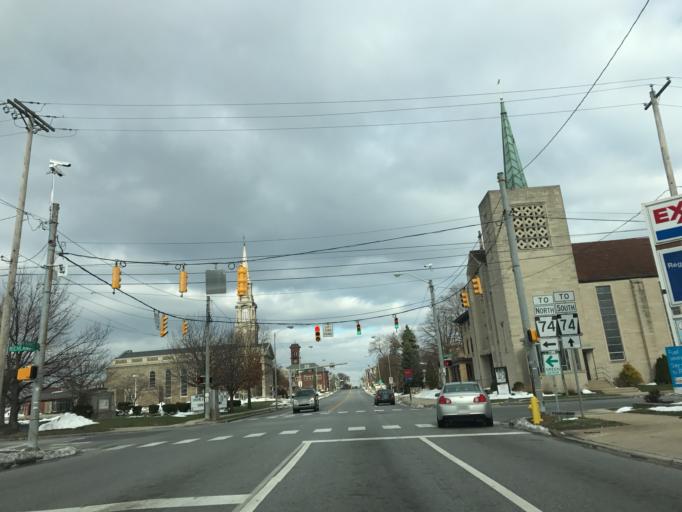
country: US
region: Pennsylvania
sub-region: York County
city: West York
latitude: 39.9554
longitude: -76.7502
